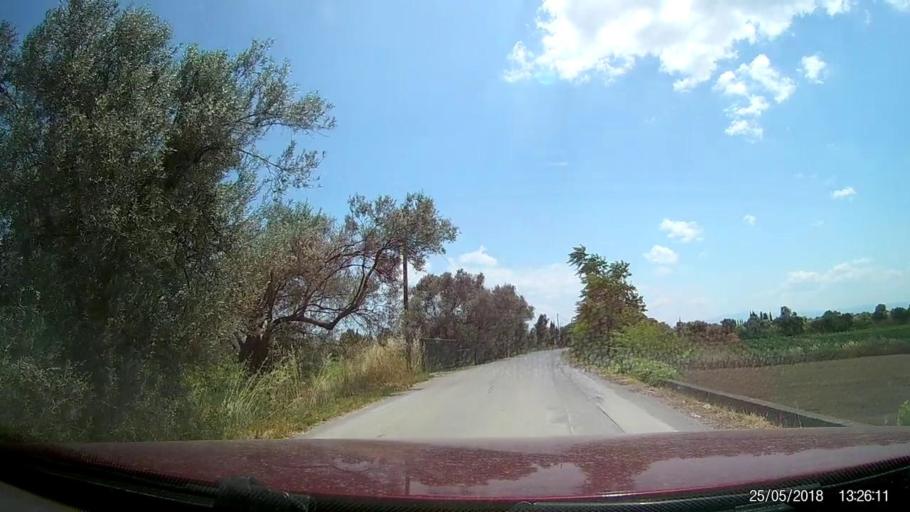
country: GR
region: Central Greece
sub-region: Nomos Evvoias
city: Mytikas
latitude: 38.4575
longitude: 23.6469
